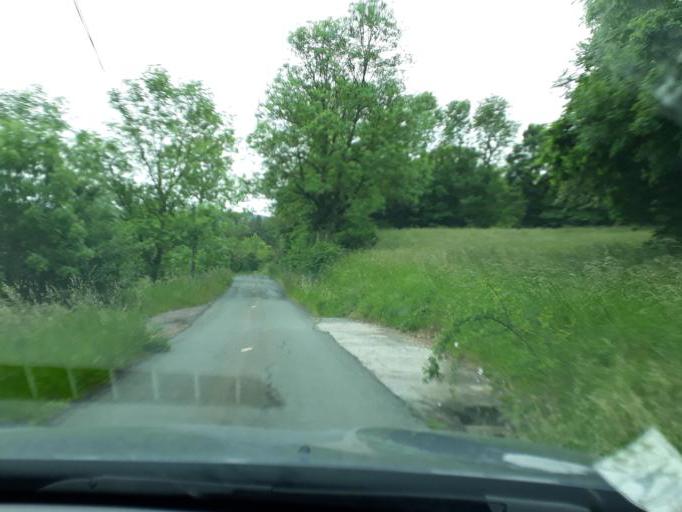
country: FR
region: Languedoc-Roussillon
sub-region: Departement de l'Herault
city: Lodeve
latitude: 43.8419
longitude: 3.2716
